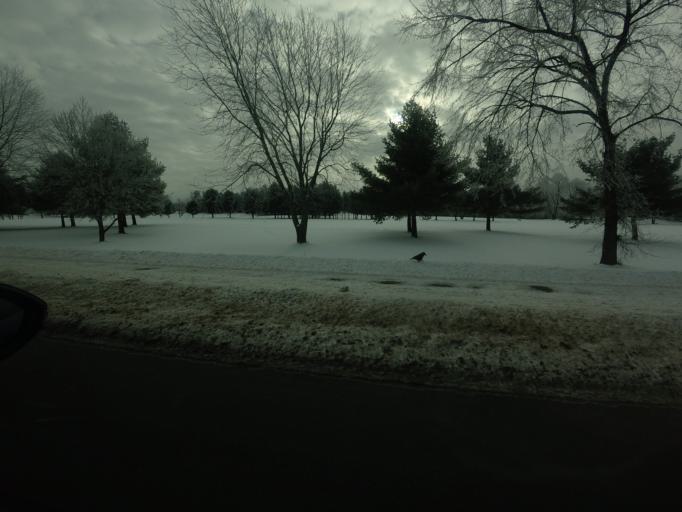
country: CA
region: New Brunswick
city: Oromocto
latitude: 45.8469
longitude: -66.5002
